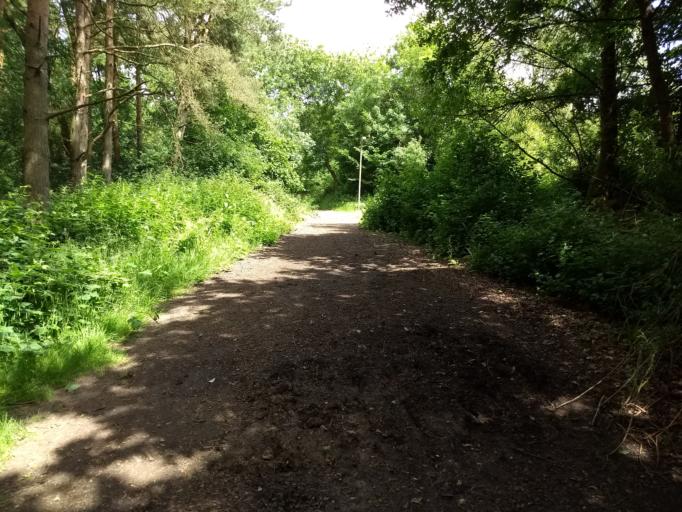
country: GB
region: England
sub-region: Milton Keynes
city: Shenley Church End
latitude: 52.0100
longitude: -0.8118
